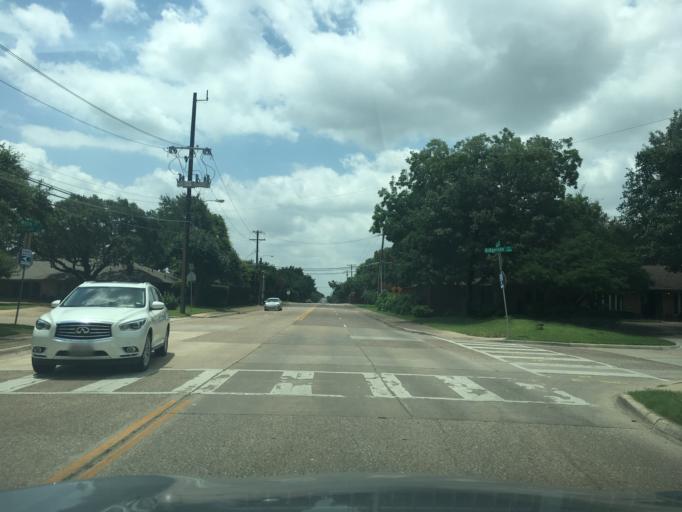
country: US
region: Texas
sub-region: Dallas County
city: Addison
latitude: 32.9156
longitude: -96.8296
